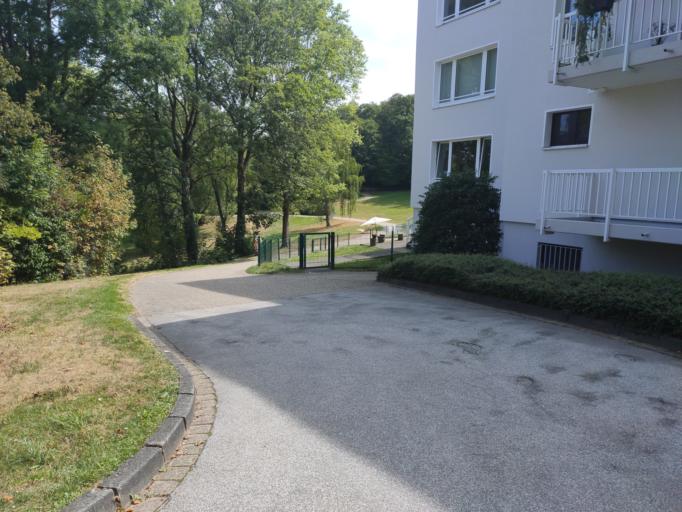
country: DE
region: North Rhine-Westphalia
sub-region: Regierungsbezirk Dusseldorf
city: Wuppertal
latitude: 51.2503
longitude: 7.1563
